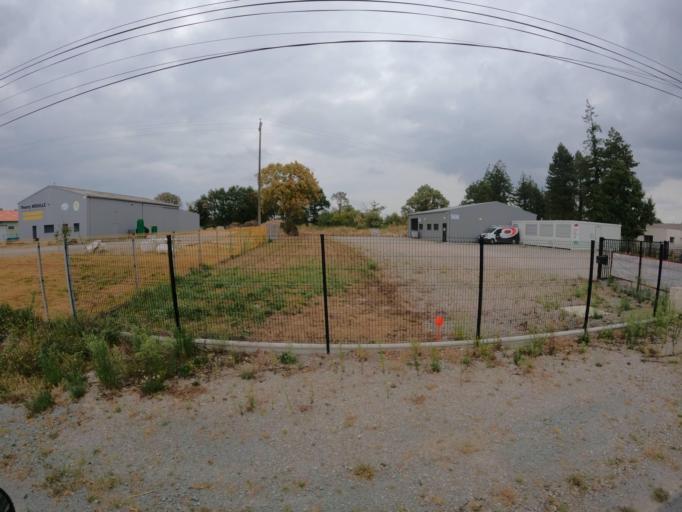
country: FR
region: Pays de la Loire
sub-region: Departement de la Vendee
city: Tiffauges
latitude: 47.0057
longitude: -1.1020
